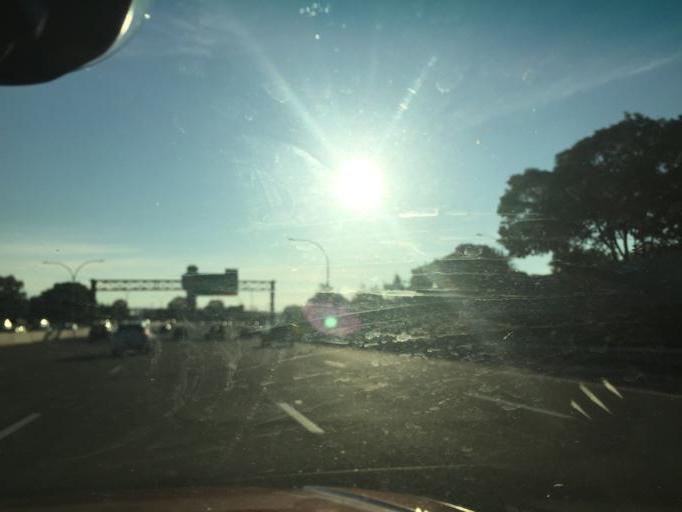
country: US
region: New York
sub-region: Queens County
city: Long Island City
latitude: 40.7696
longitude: -73.8804
